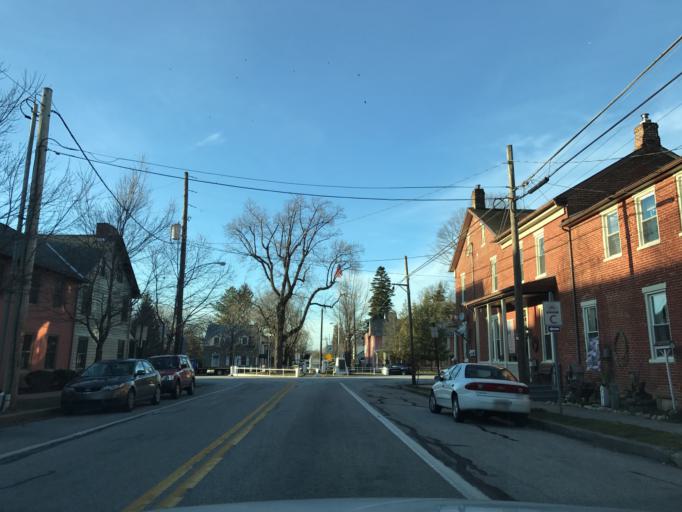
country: US
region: Pennsylvania
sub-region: Lancaster County
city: Maytown
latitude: 40.0750
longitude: -76.5817
